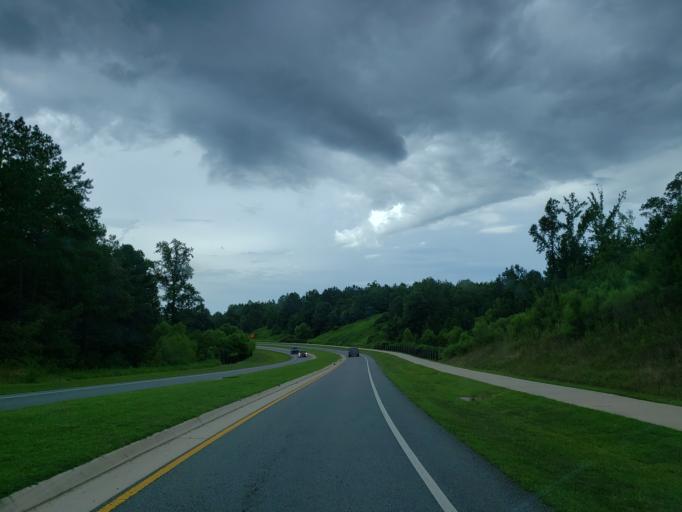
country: US
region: Georgia
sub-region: Cobb County
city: Acworth
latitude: 34.0306
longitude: -84.7678
